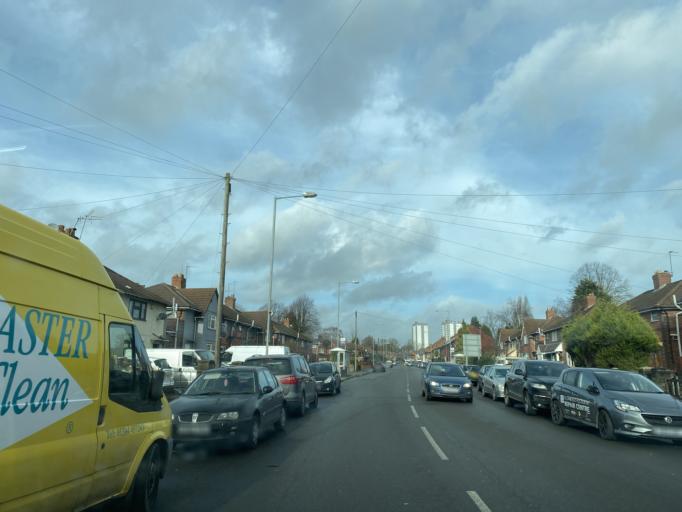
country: GB
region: England
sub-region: Walsall
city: Walsall
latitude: 52.5686
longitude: -1.9808
